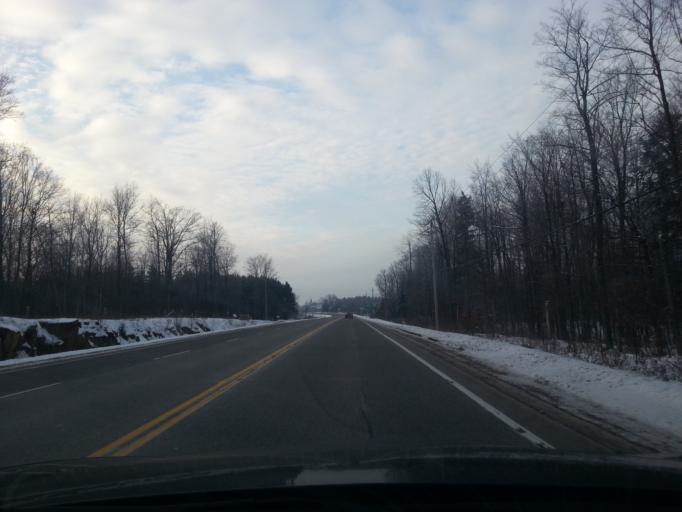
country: CA
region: Ontario
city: Carleton Place
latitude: 45.0917
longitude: -76.2418
